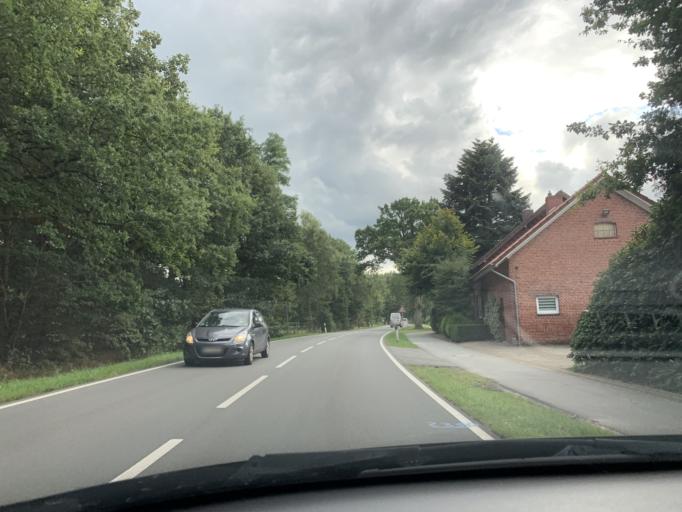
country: DE
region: Lower Saxony
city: Westerstede
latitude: 53.2901
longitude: 7.9226
